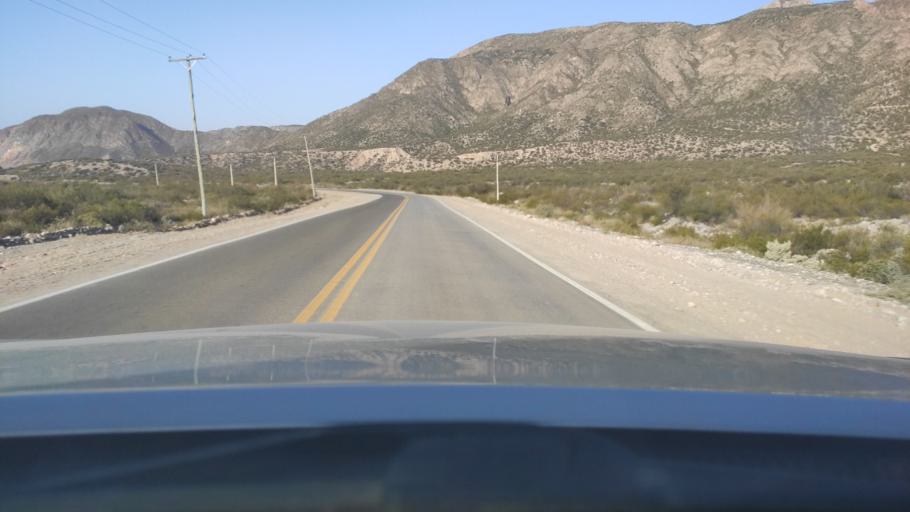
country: AR
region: San Juan
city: Villa Media Agua
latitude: -32.0085
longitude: -68.7727
